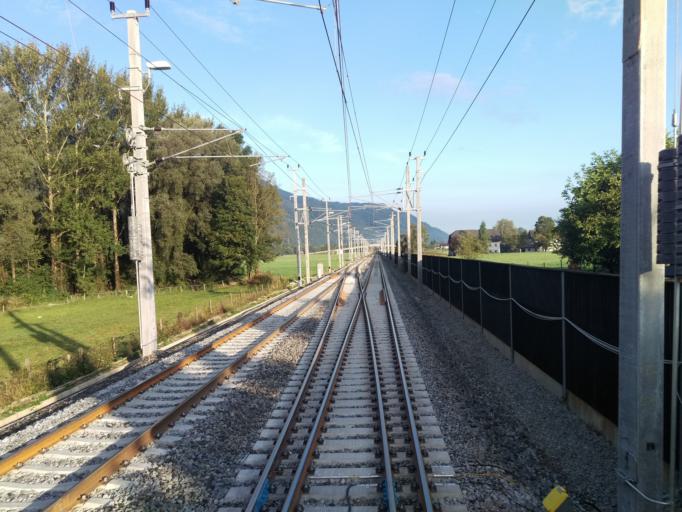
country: AT
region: Salzburg
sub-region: Politischer Bezirk Hallein
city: Golling an der Salzach
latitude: 47.6091
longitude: 13.1590
